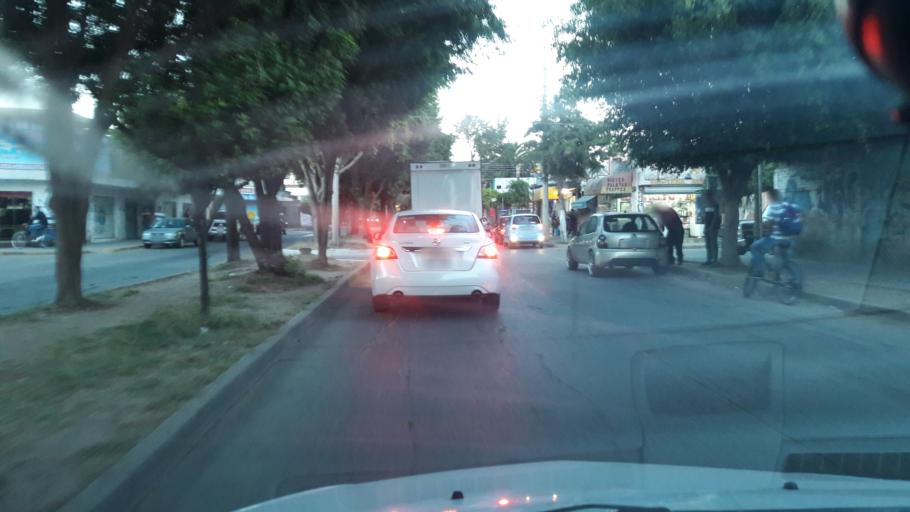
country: MX
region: Guanajuato
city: Leon
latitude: 21.1702
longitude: -101.6670
